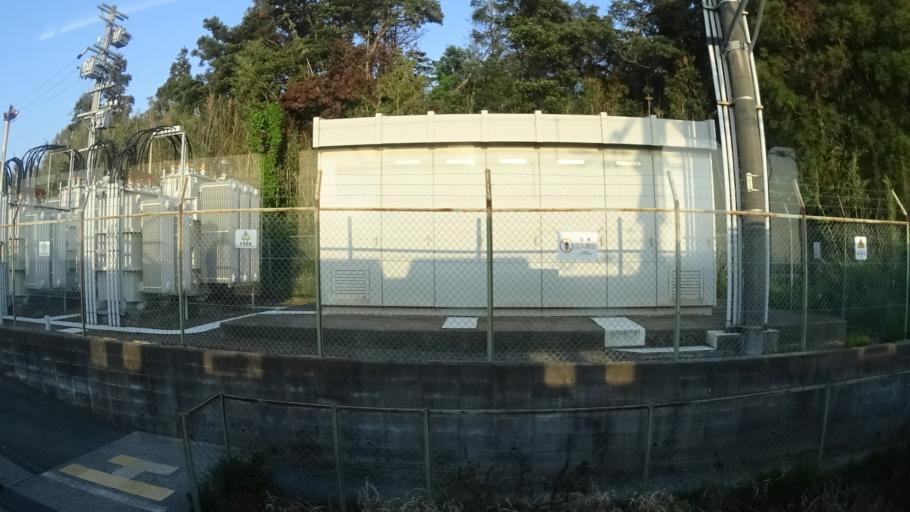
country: JP
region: Aichi
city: Tahara
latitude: 34.6799
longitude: 137.3206
